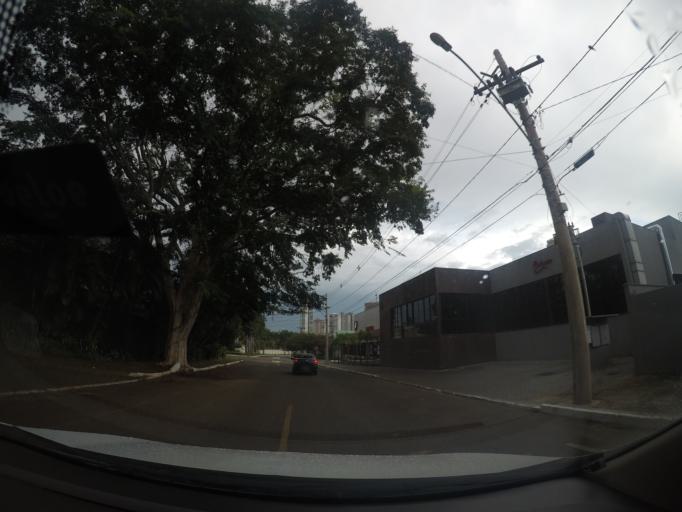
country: BR
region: Goias
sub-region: Goiania
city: Goiania
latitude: -16.7030
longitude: -49.2599
